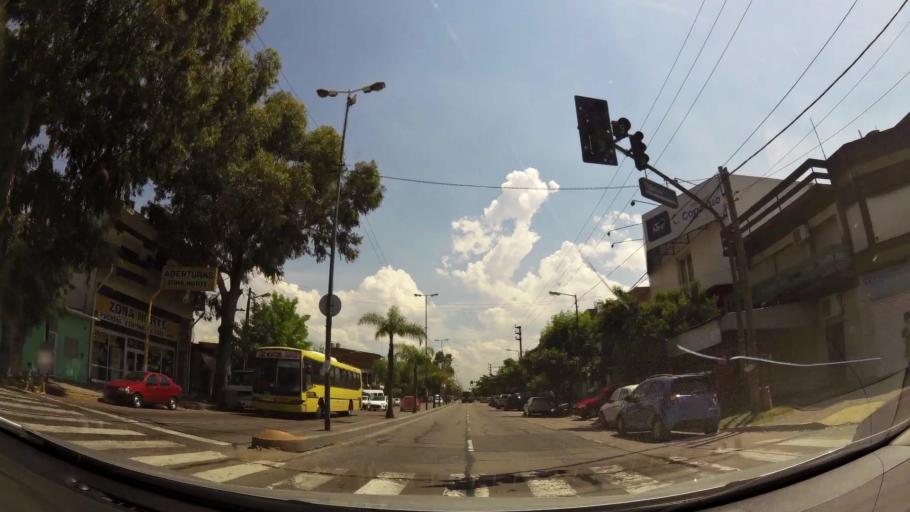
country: AR
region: Buenos Aires
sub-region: Partido de Tigre
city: Tigre
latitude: -34.4652
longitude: -58.5817
